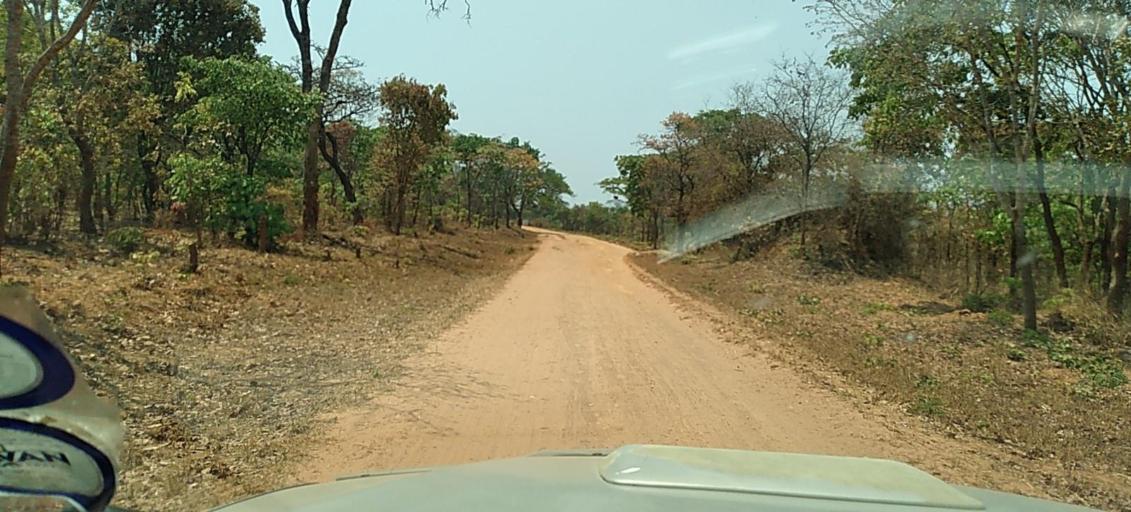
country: ZM
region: North-Western
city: Kasempa
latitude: -13.5509
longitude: 26.0246
